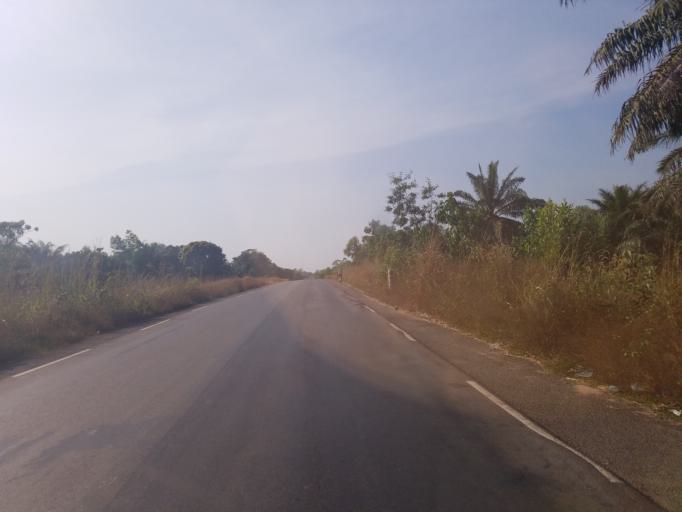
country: GN
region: Boke
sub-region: Boffa
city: Boffa
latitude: 10.1901
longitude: -14.0506
